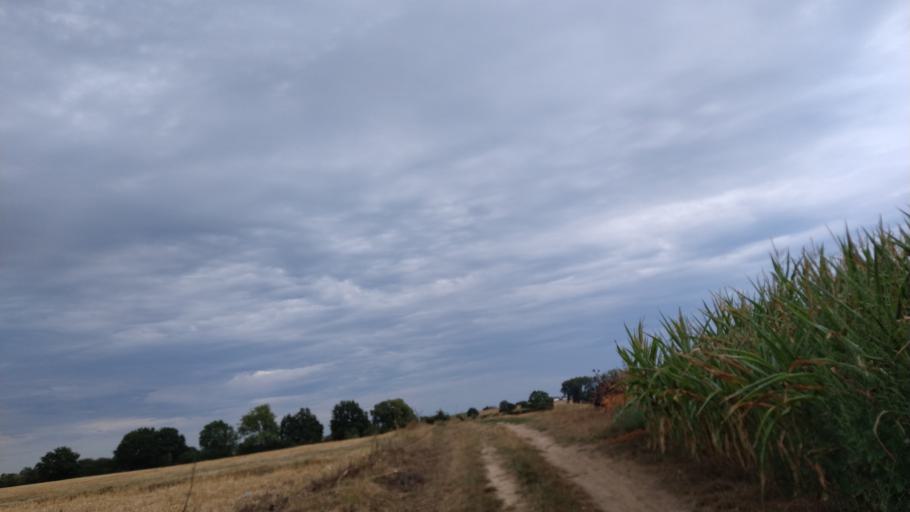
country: BE
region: Flanders
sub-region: Provincie Vlaams-Brabant
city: Tervuren
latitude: 50.8501
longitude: 4.5238
